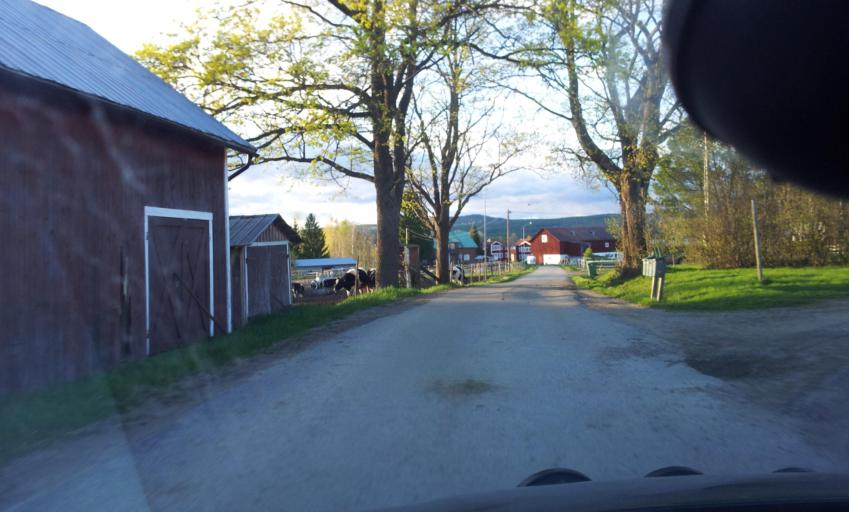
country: SE
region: Gaevleborg
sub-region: Bollnas Kommun
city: Kilafors
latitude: 61.3836
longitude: 16.6237
